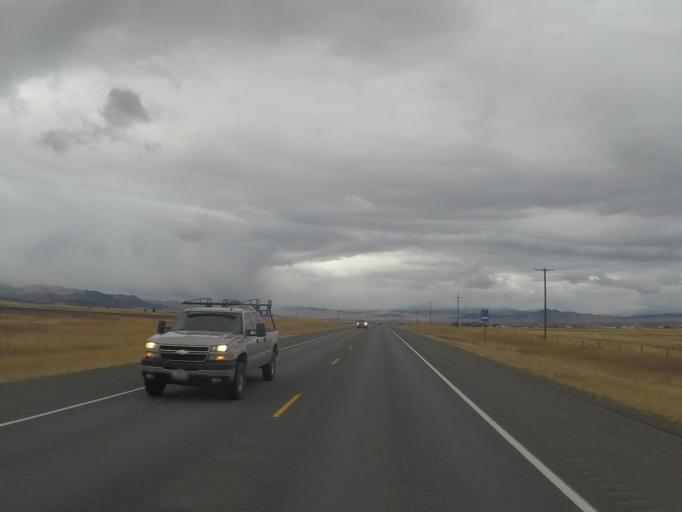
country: US
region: Montana
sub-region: Lewis and Clark County
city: East Helena
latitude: 46.5849
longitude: -111.8636
